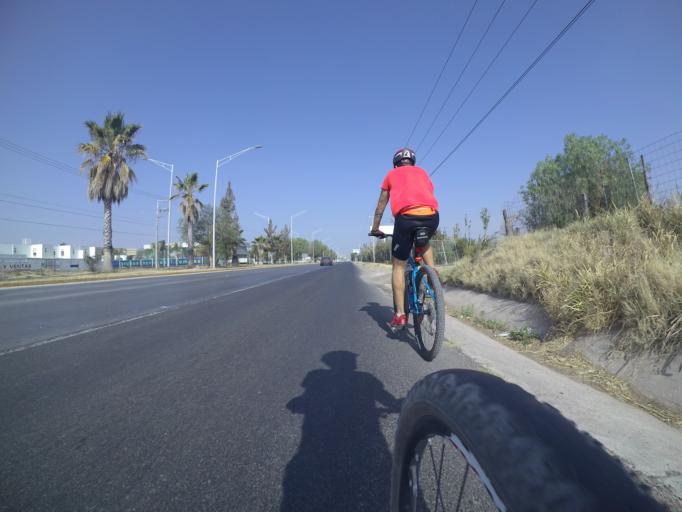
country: MX
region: Aguascalientes
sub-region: Jesus Maria
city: Arboledas Paso Blanco [Fraccionamiento]
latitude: 21.9467
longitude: -102.3010
